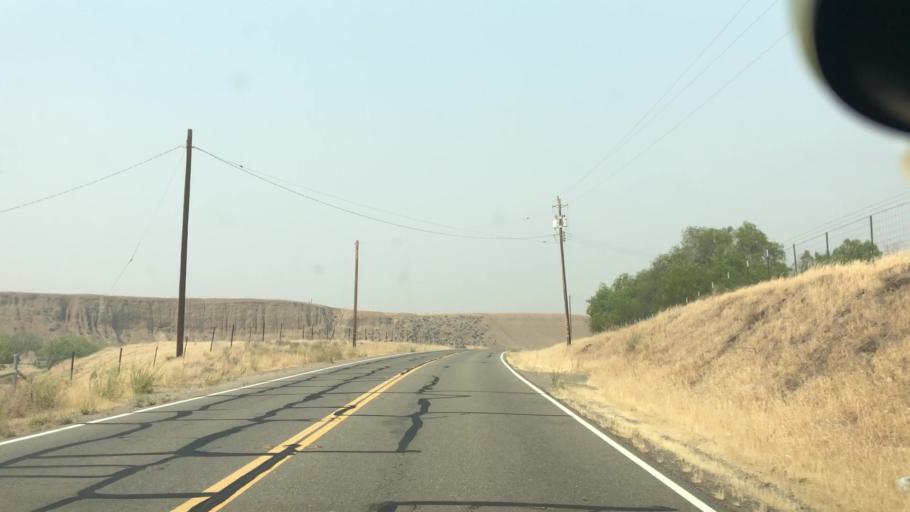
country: US
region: California
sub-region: San Joaquin County
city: Tracy
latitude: 37.6607
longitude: -121.4717
